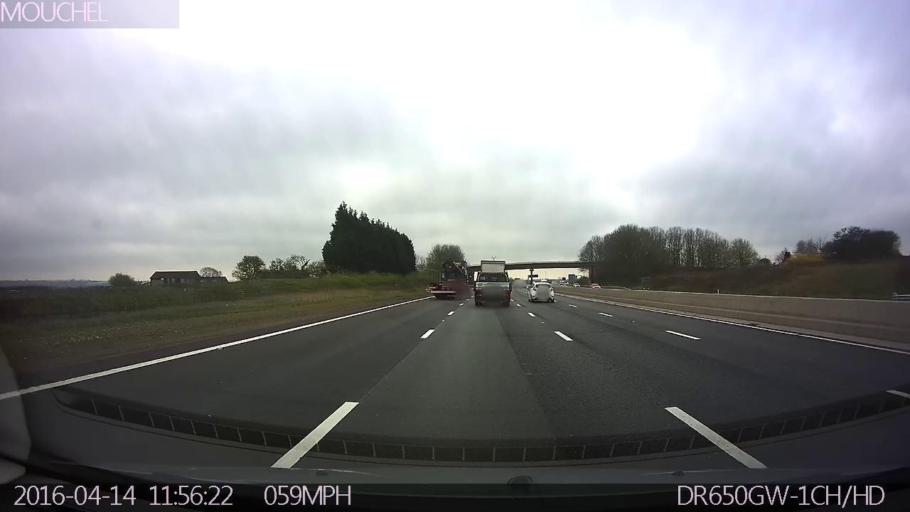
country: GB
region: England
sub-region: Derbyshire
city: Blackwell
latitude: 53.1316
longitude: -1.3289
